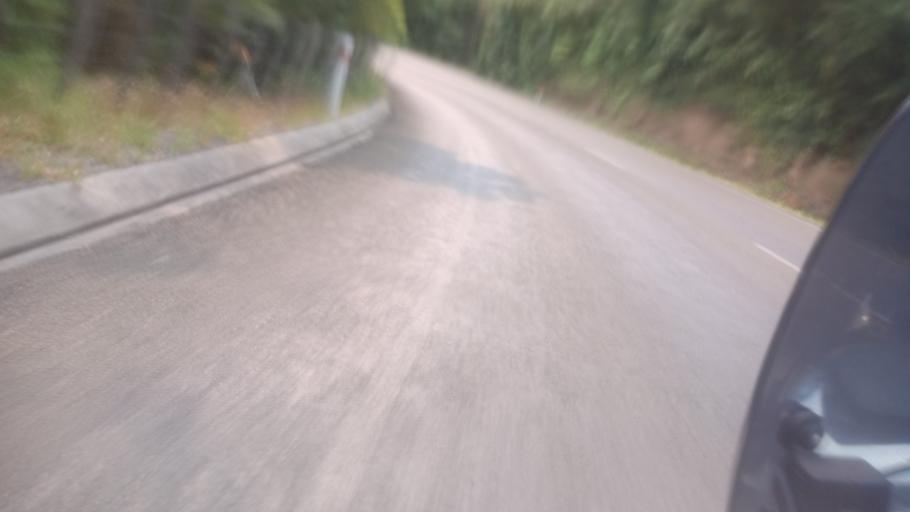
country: NZ
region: Bay of Plenty
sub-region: Opotiki District
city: Opotiki
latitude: -37.9656
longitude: 177.4616
